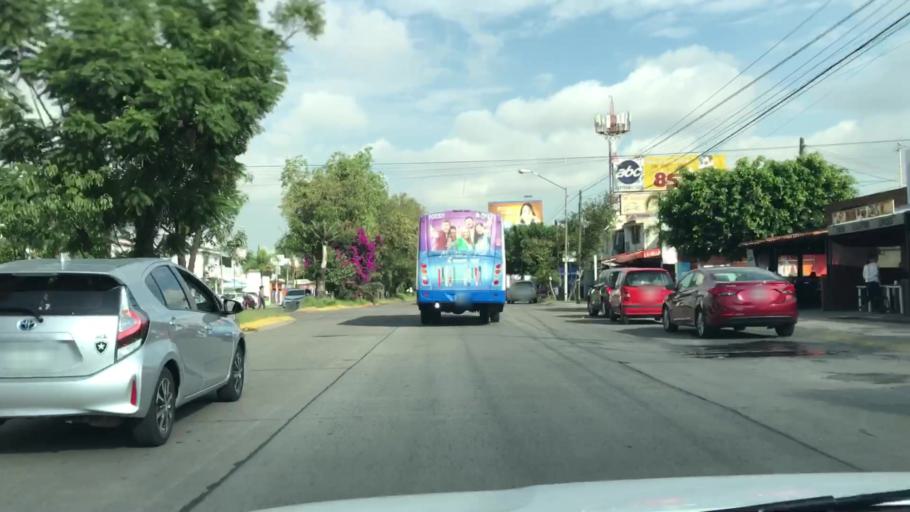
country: MX
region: Jalisco
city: Guadalajara
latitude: 20.6354
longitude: -103.4268
